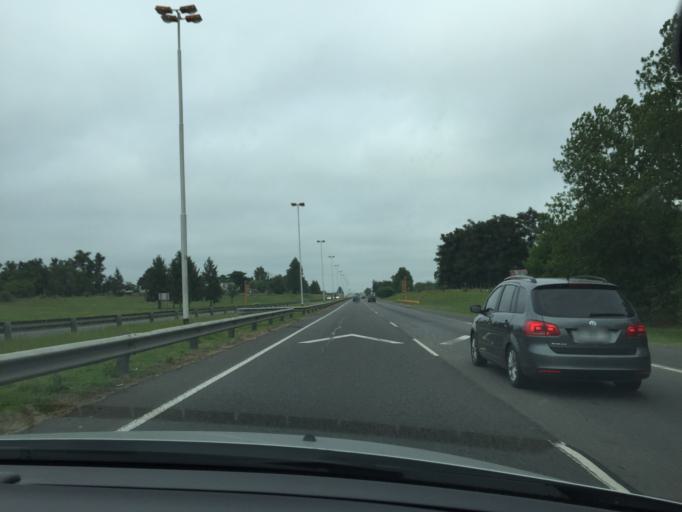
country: AR
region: Buenos Aires
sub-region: Partido de Ezeiza
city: Ezeiza
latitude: -34.8348
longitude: -58.5143
